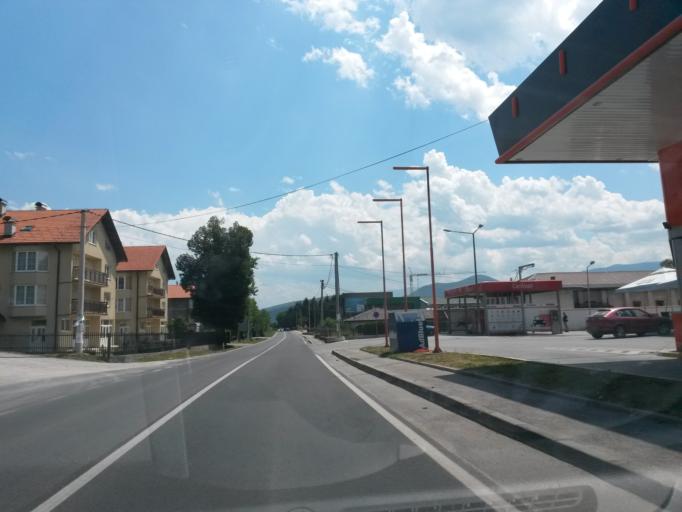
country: BA
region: Federation of Bosnia and Herzegovina
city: Travnik
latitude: 44.2180
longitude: 17.6938
